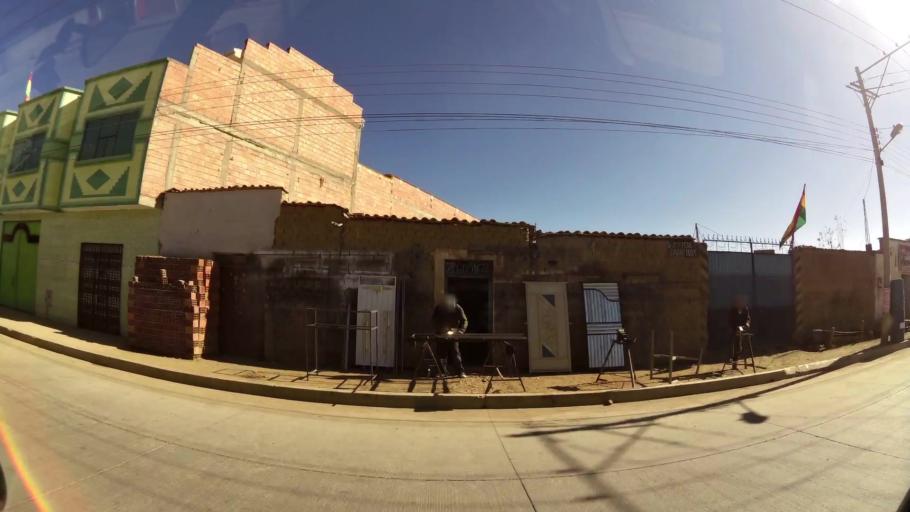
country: BO
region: La Paz
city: La Paz
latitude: -16.5277
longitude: -68.2283
